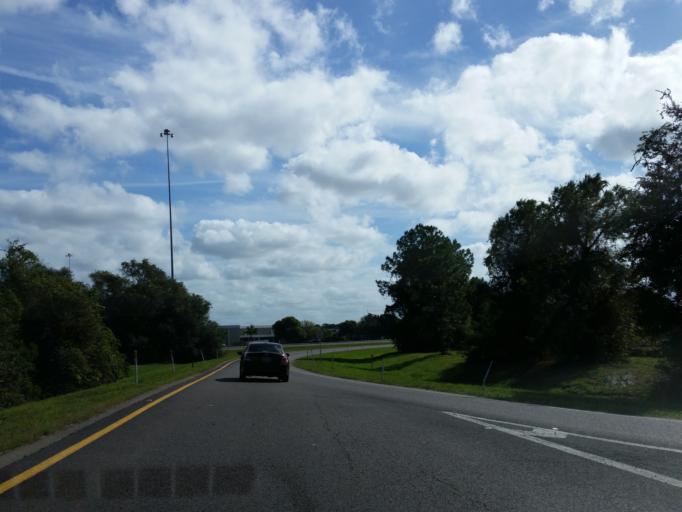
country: US
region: Florida
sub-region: Hillsborough County
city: Riverview
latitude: 27.8500
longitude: -82.3487
